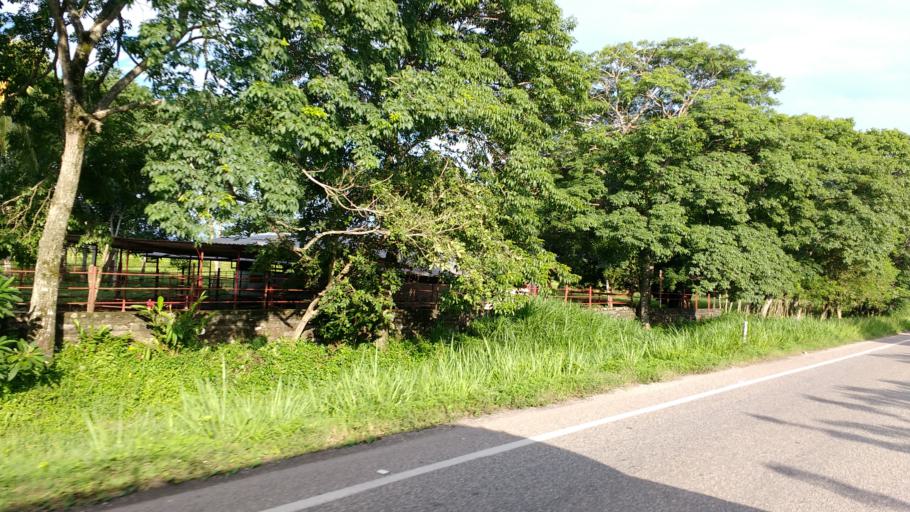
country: MX
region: Tabasco
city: Teapa
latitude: 17.6022
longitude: -92.9645
